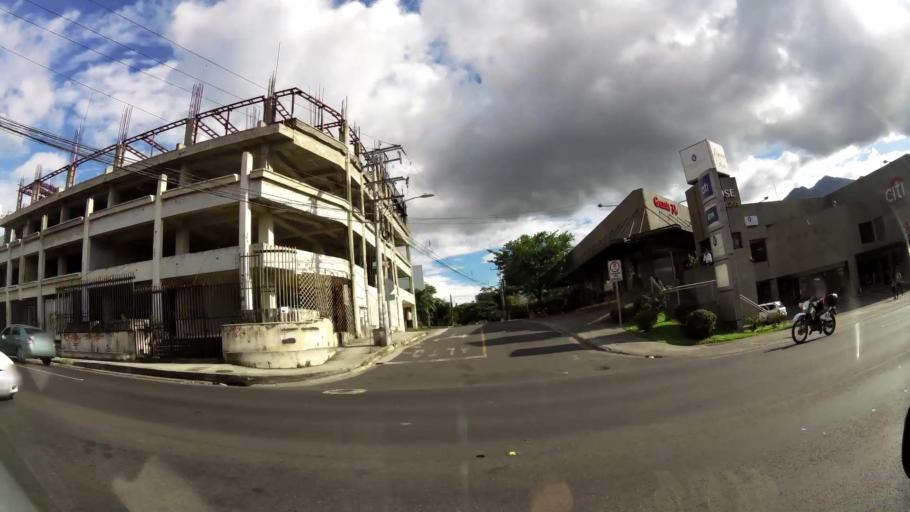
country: CR
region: San Jose
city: San Rafael
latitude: 9.9313
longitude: -84.1309
